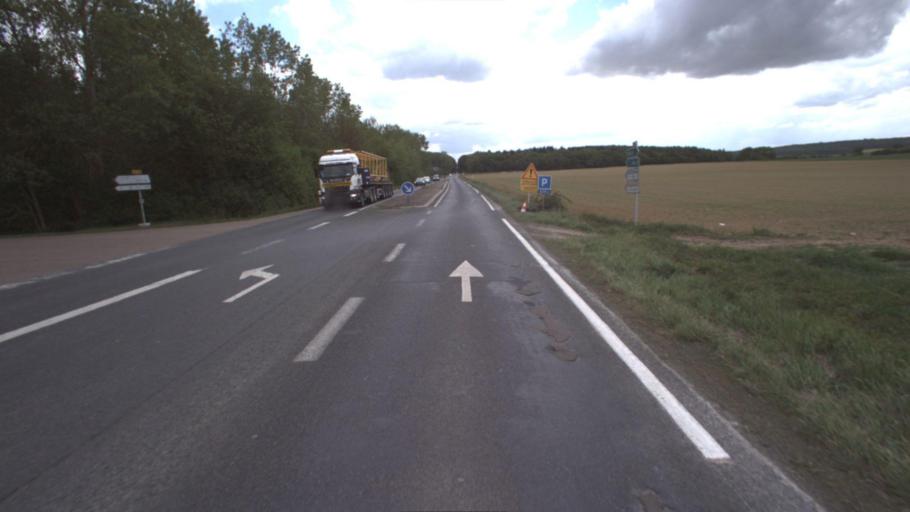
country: FR
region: Ile-de-France
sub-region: Departement de Seine-et-Marne
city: Saint-Pathus
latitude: 49.0639
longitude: 2.7761
